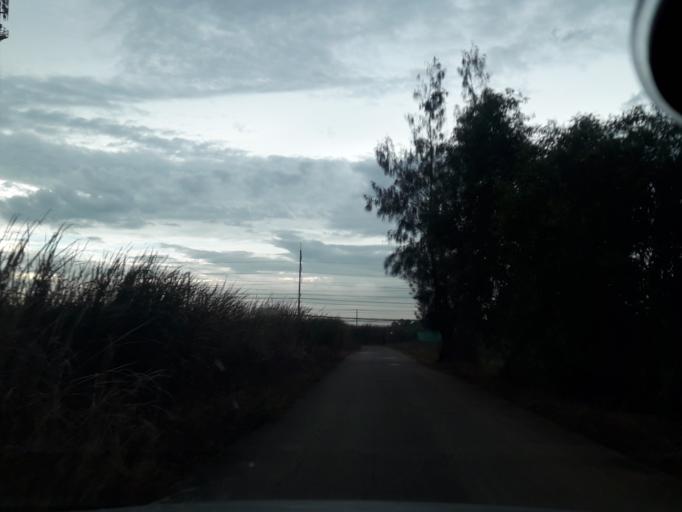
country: TH
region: Phra Nakhon Si Ayutthaya
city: Wang Noi
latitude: 14.2614
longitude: 100.7817
